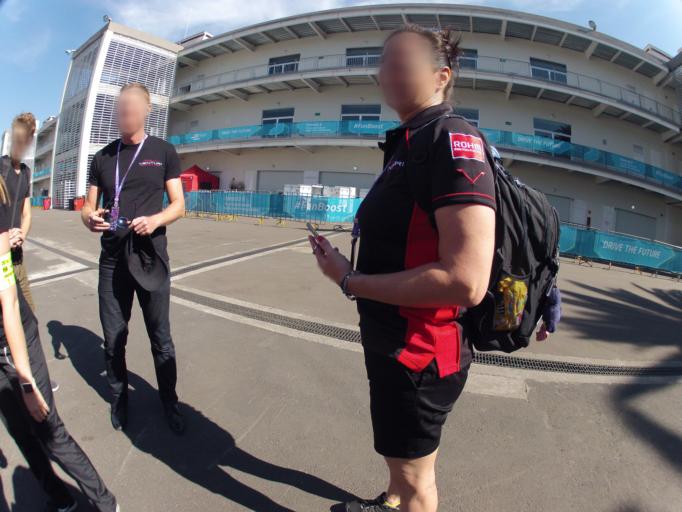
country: MX
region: Mexico City
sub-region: Iztacalco
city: Iztacalco
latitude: 19.4054
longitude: -99.0935
